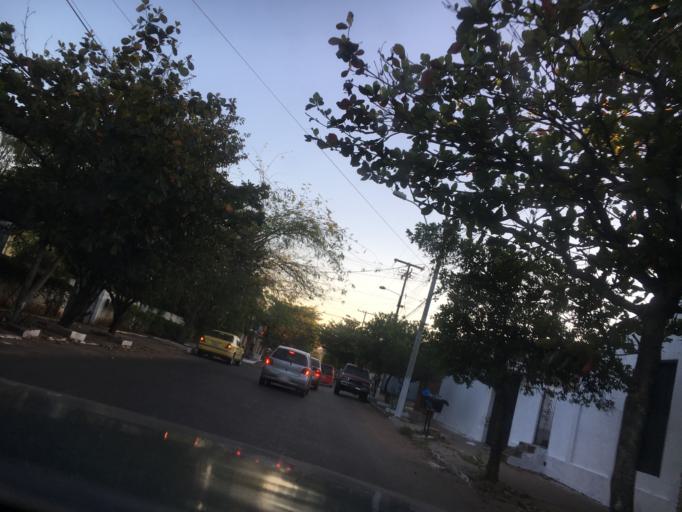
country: PY
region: Central
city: Lambare
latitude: -25.3216
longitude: -57.6109
